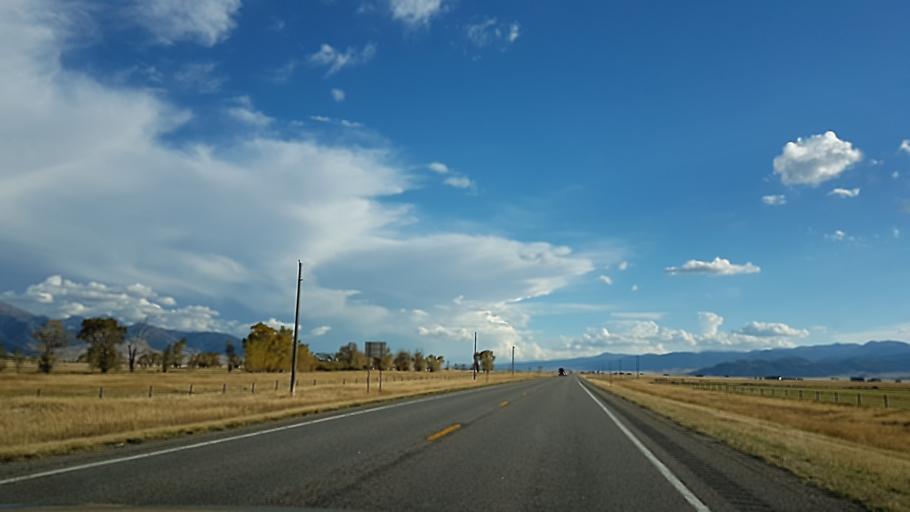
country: US
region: Montana
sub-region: Madison County
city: Virginia City
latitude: 45.1984
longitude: -111.6788
